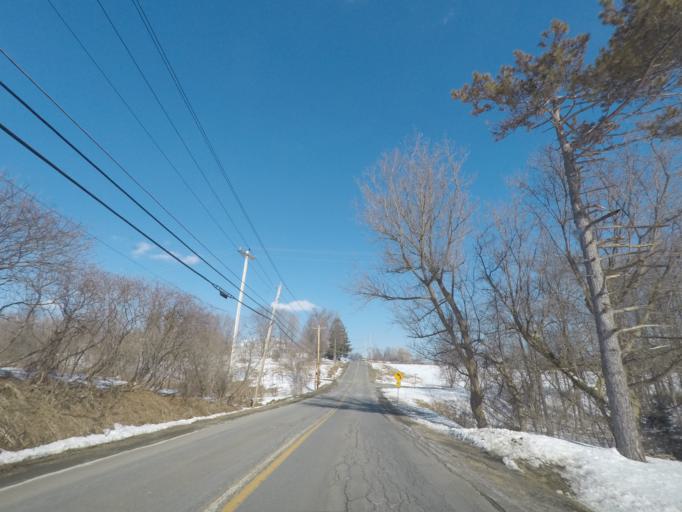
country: US
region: New York
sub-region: Saratoga County
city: Stillwater
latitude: 42.9098
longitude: -73.5679
